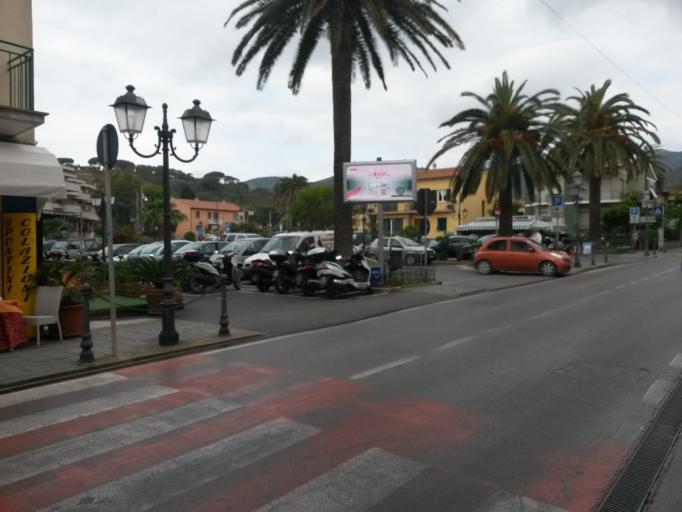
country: IT
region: Tuscany
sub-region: Provincia di Livorno
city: Porto Azzurro
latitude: 42.7655
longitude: 10.3954
